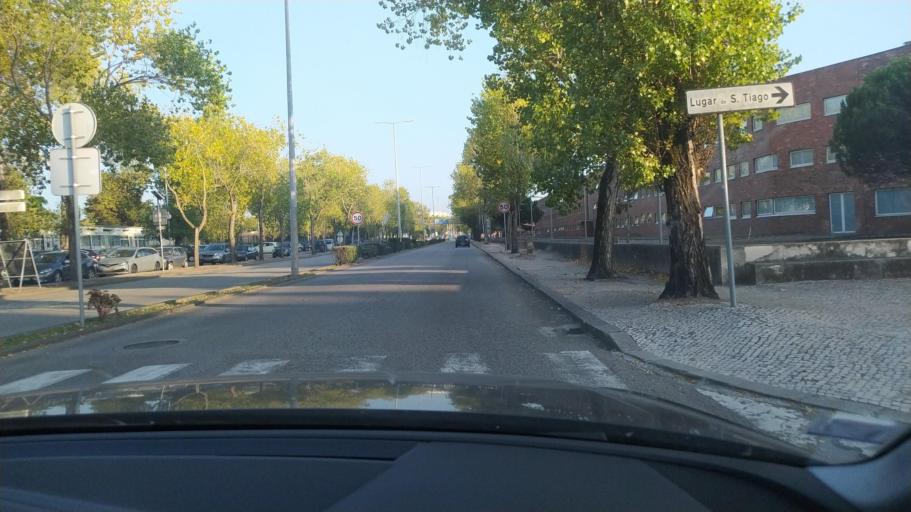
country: PT
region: Aveiro
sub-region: Aveiro
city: Aveiro
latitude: 40.6331
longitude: -8.6558
